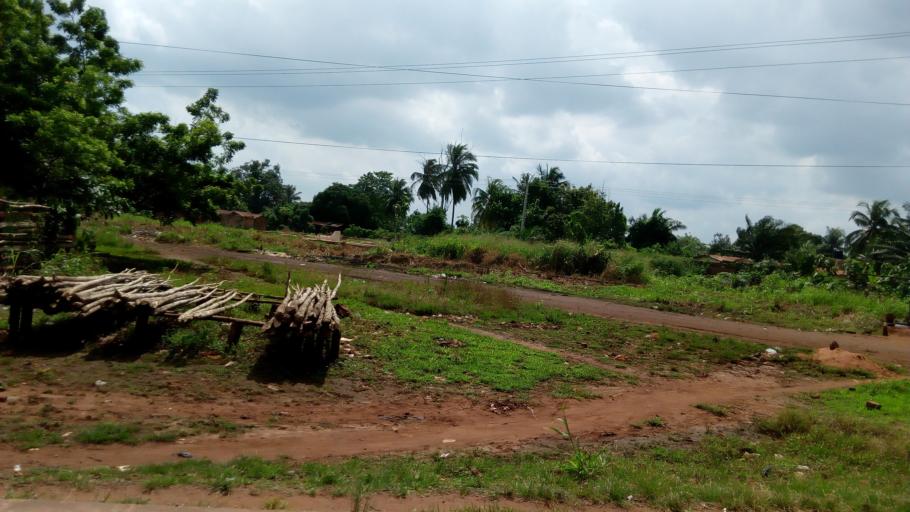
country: TG
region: Maritime
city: Tsevie
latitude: 6.4354
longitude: 1.2117
